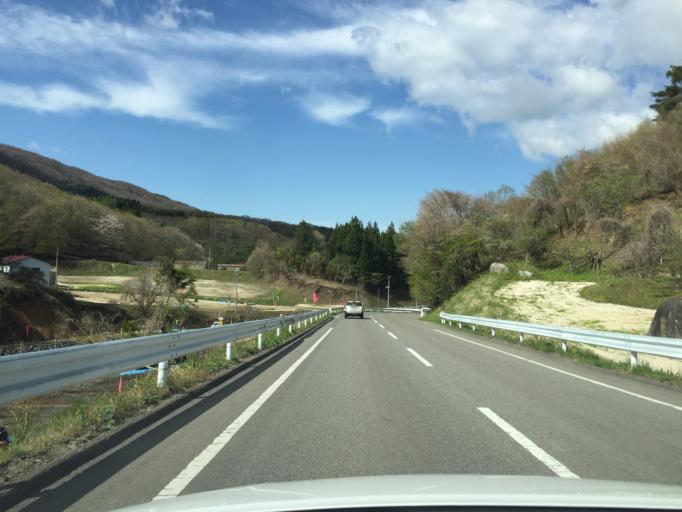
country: JP
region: Fukushima
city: Funehikimachi-funehiki
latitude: 37.5626
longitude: 140.6875
